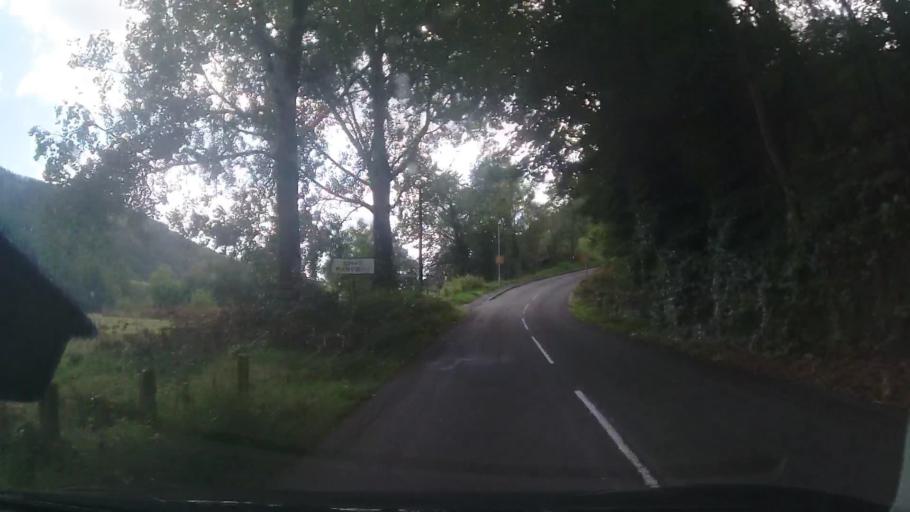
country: GB
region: Wales
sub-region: Gwynedd
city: Corris
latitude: 52.7204
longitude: -3.6896
